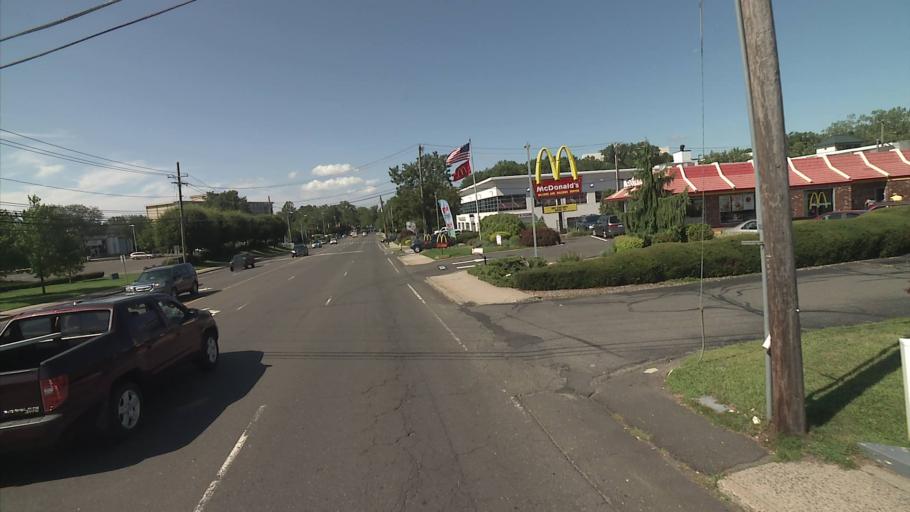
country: US
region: Connecticut
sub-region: Fairfield County
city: Darien
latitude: 41.0937
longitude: -73.4513
